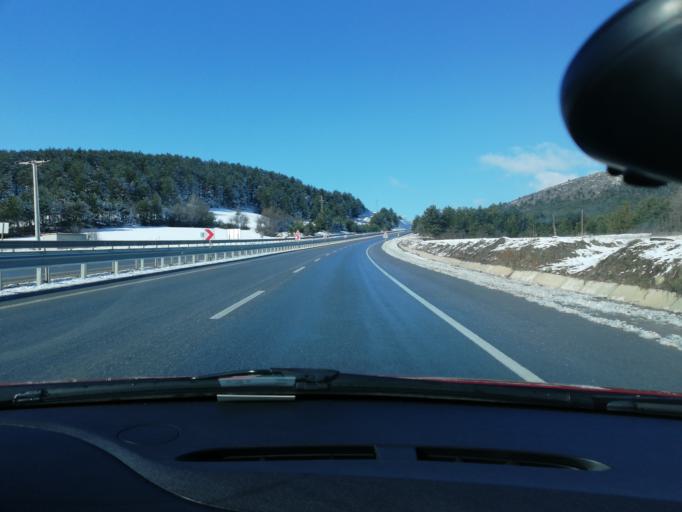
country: TR
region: Kastamonu
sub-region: Cide
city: Kastamonu
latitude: 41.3604
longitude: 33.7060
